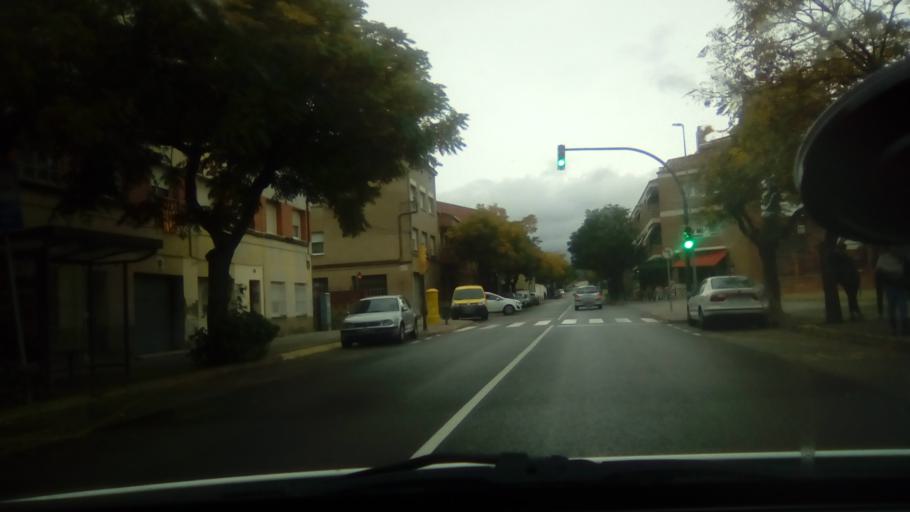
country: ES
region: Catalonia
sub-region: Provincia de Barcelona
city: Monistrol de Montserrat
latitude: 41.6707
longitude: 1.8627
